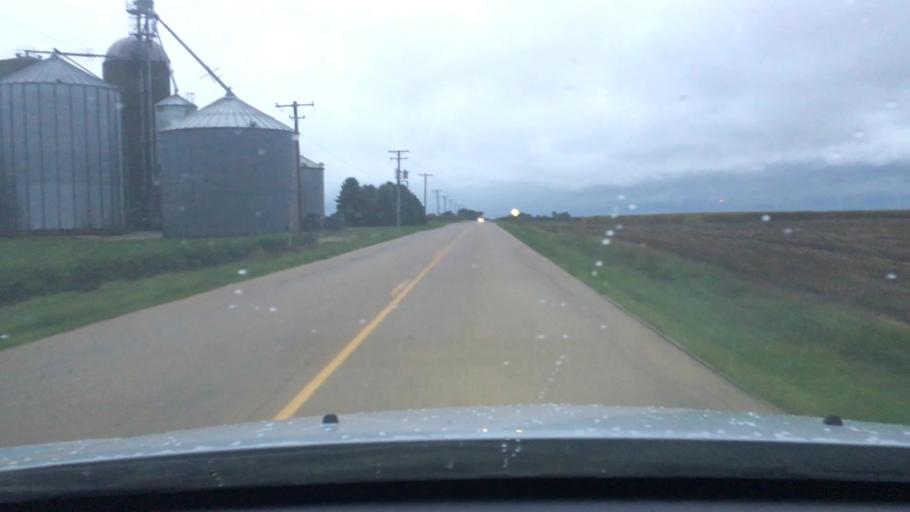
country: US
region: Illinois
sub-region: DeKalb County
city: Malta
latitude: 41.8519
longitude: -88.9612
